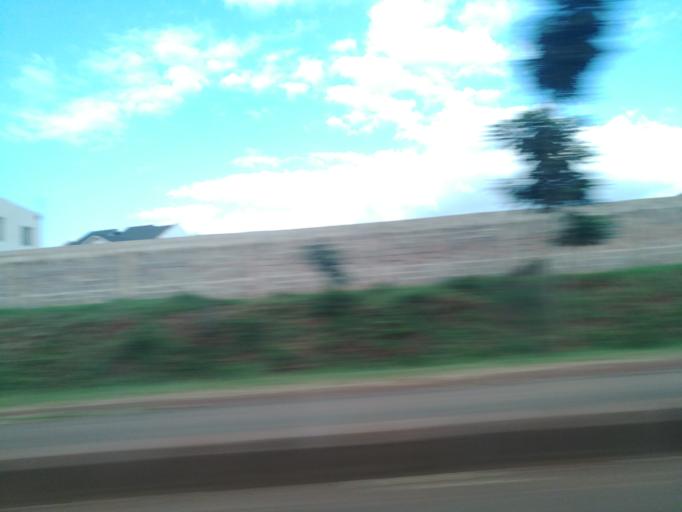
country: KE
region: Nairobi Area
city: Thika
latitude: -1.0359
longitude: 37.0645
